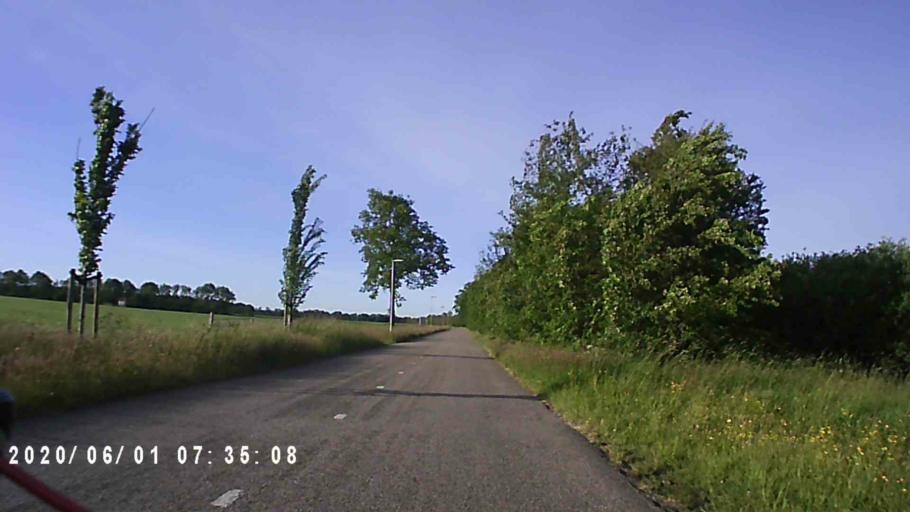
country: NL
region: Friesland
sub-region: Gemeente Dongeradeel
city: Dokkum
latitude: 53.3074
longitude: 5.9944
